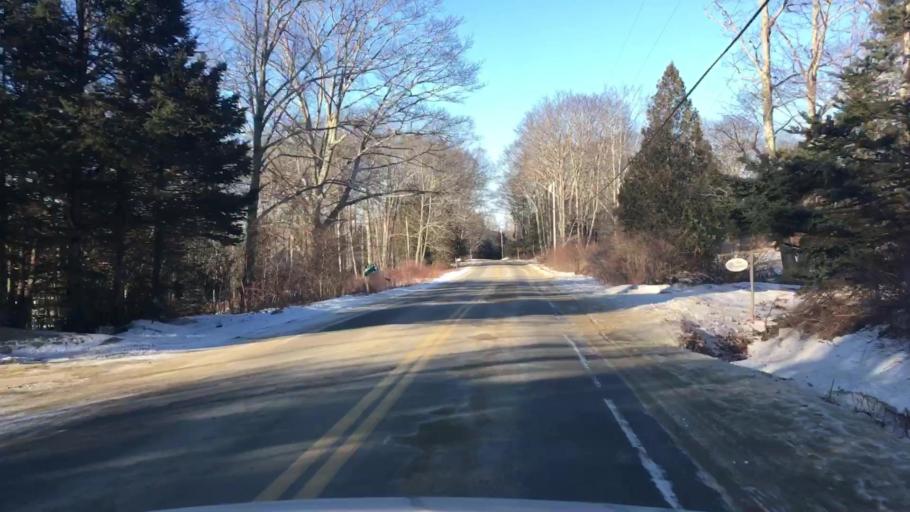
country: US
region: Maine
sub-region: Hancock County
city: Castine
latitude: 44.3737
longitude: -68.7523
